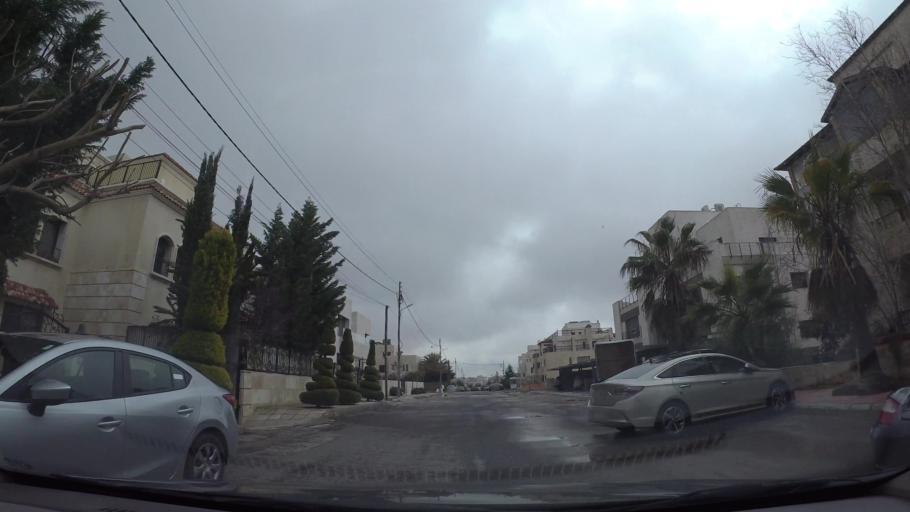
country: JO
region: Amman
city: Al Bunayyat ash Shamaliyah
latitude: 31.9343
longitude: 35.8890
